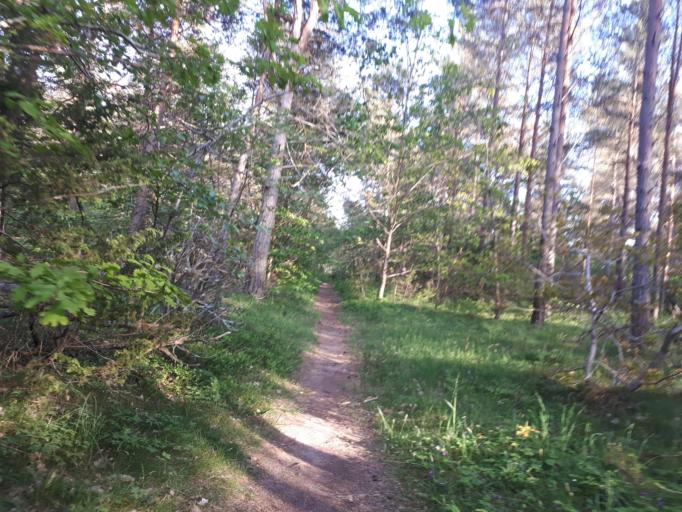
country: SE
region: Gotland
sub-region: Gotland
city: Visby
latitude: 57.6081
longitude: 18.2956
